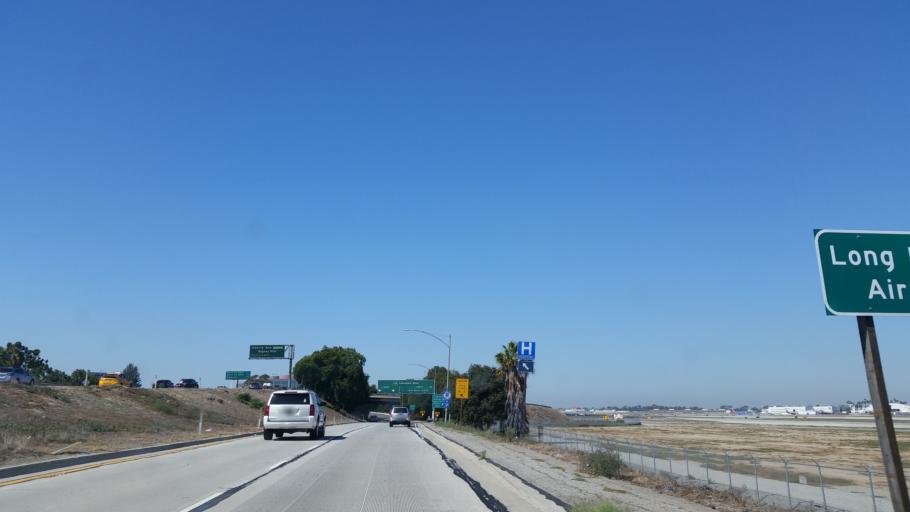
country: US
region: California
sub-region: Los Angeles County
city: Signal Hill
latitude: 33.8041
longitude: -118.1385
